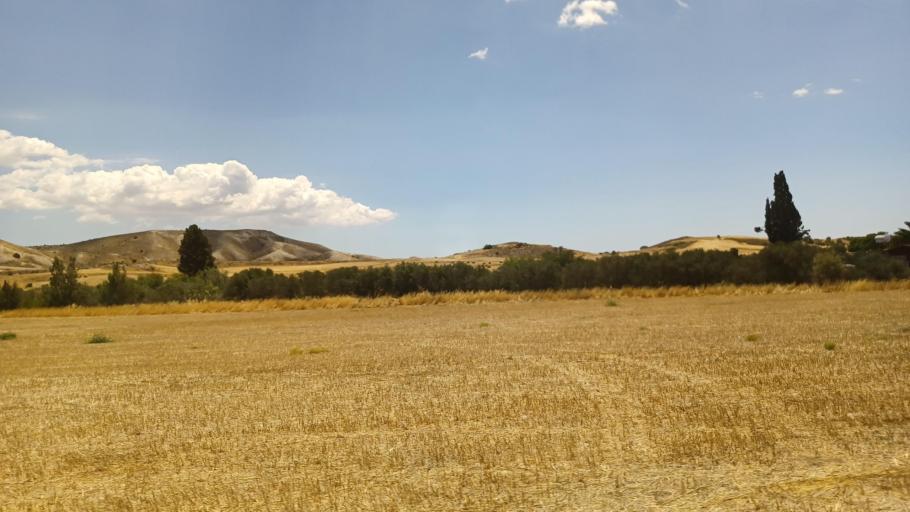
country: CY
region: Larnaka
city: Troulloi
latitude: 35.0410
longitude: 33.6171
